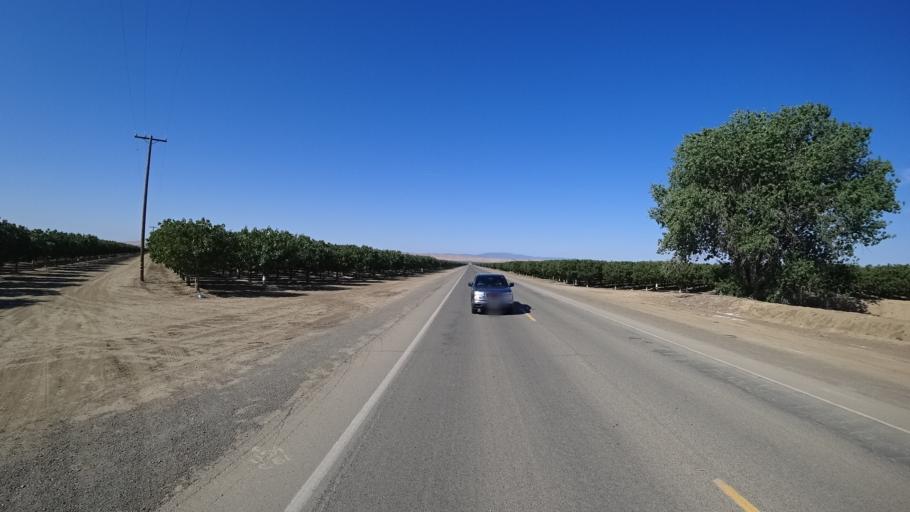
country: US
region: California
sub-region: Fresno County
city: Huron
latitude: 36.1226
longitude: -120.0307
